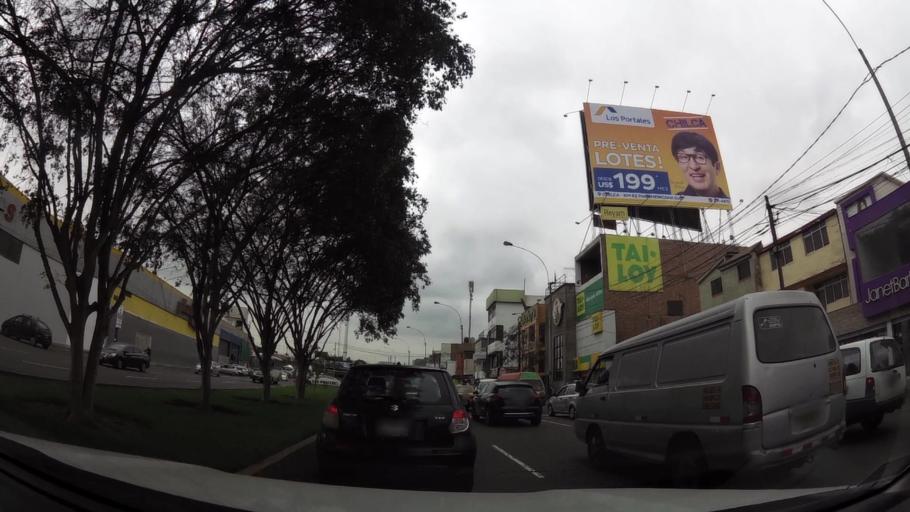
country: PE
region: Lima
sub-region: Lima
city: Surco
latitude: -12.1495
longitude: -76.9871
